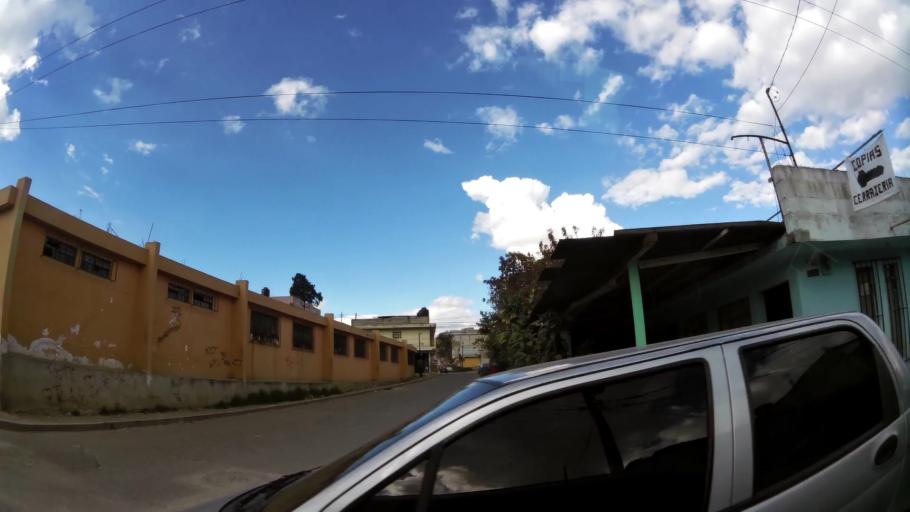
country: GT
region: Quetzaltenango
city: Quetzaltenango
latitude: 14.8518
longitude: -91.5175
